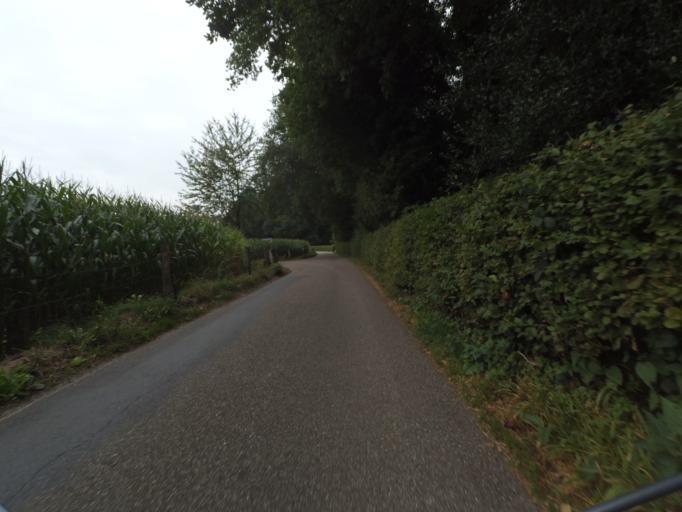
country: NL
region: Overijssel
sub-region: Gemeente Oldenzaal
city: Oldenzaal
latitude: 52.3174
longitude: 6.9664
